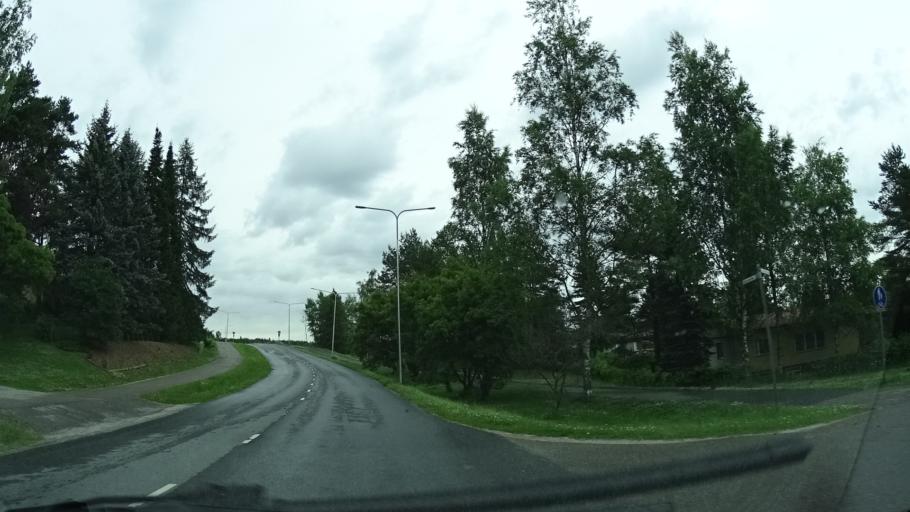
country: FI
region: Varsinais-Suomi
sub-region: Salo
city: Halikko
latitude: 60.4031
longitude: 23.0798
